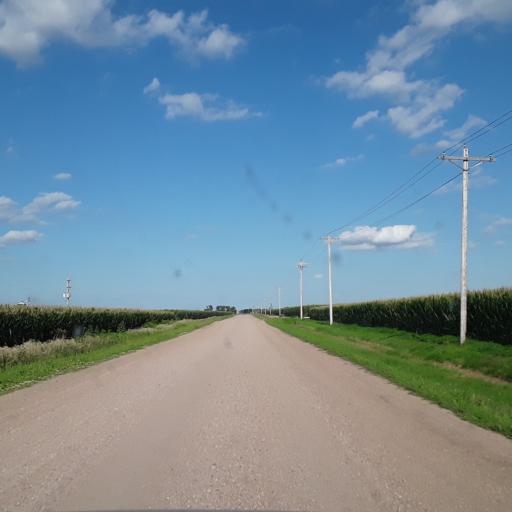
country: US
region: Nebraska
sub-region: Hall County
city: Wood River
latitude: 40.9168
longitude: -98.5808
